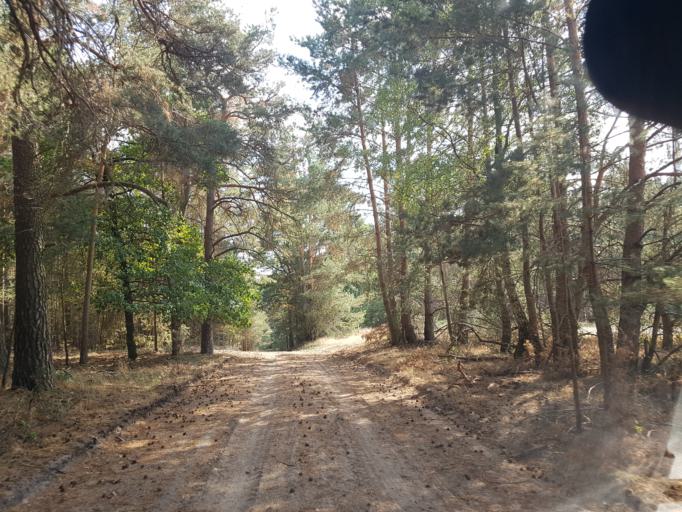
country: DE
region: Brandenburg
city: Treuenbrietzen
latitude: 52.0194
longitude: 12.8632
